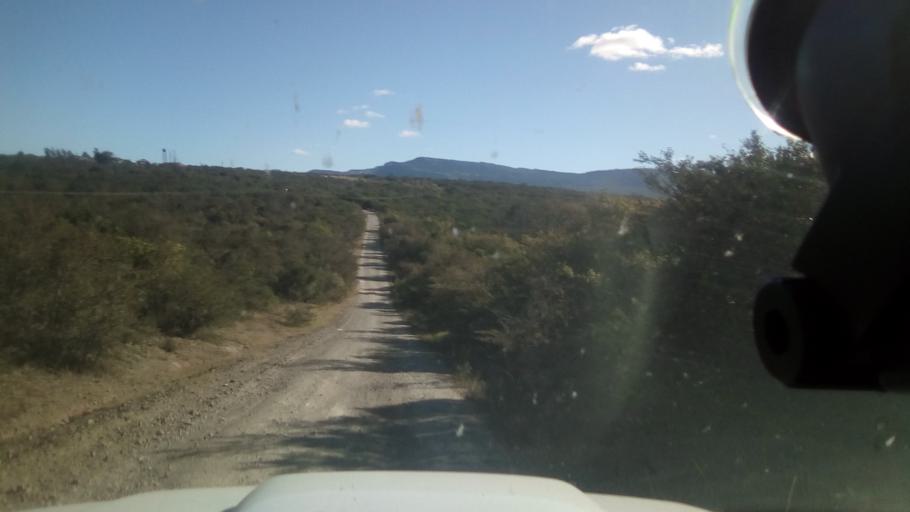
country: ZA
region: Eastern Cape
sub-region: Buffalo City Metropolitan Municipality
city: Bhisho
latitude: -32.7527
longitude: 27.3430
